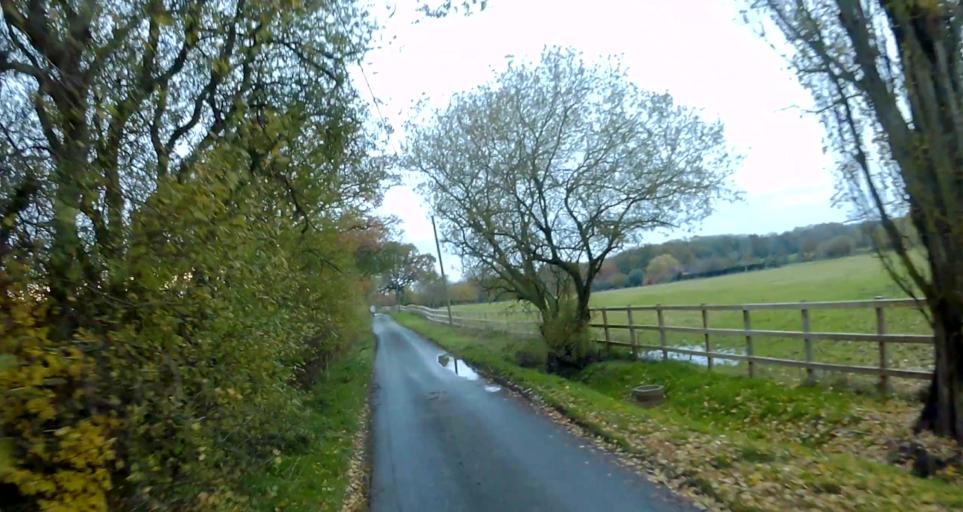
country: GB
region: England
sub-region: Hampshire
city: Odiham
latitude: 51.2488
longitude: -0.9134
